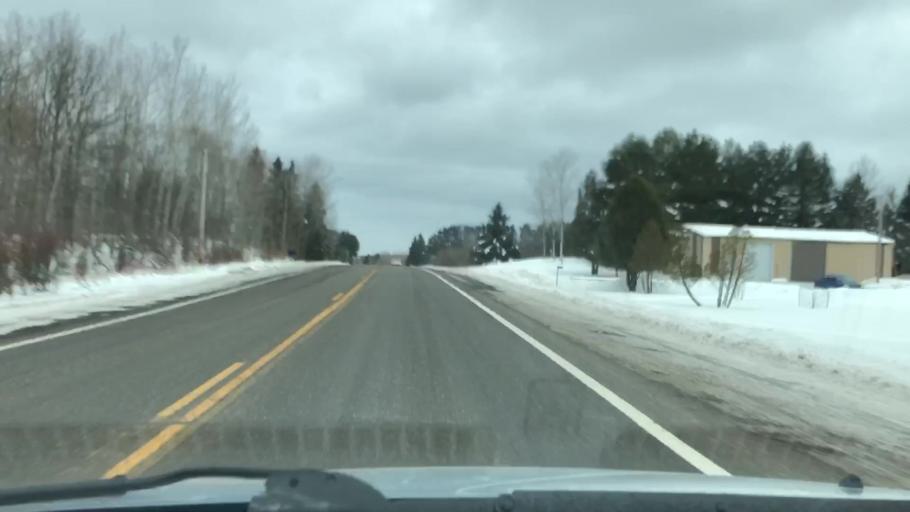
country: US
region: Minnesota
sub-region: Carlton County
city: Esko
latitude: 46.6811
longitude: -92.3704
